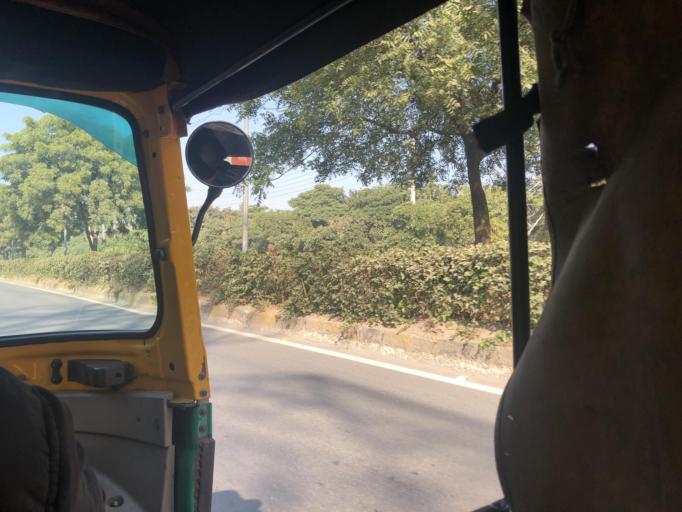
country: IN
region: Haryana
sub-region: Gurgaon
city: Gurgaon
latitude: 28.4443
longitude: 77.0828
